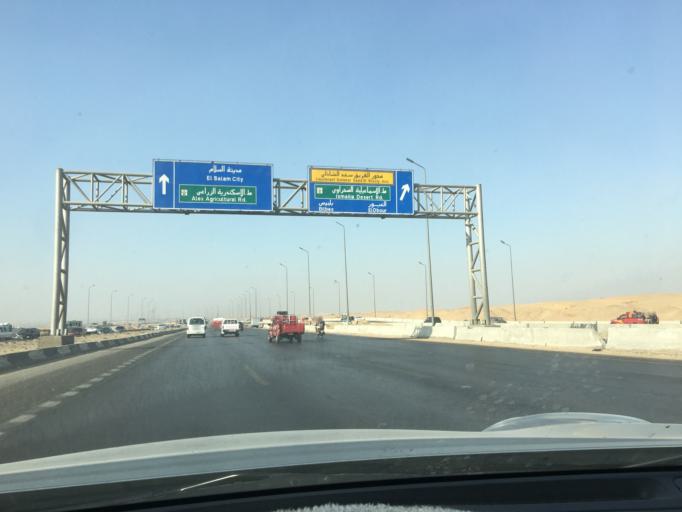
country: EG
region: Muhafazat al Qalyubiyah
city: Al Khankah
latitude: 30.1204
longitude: 31.4624
